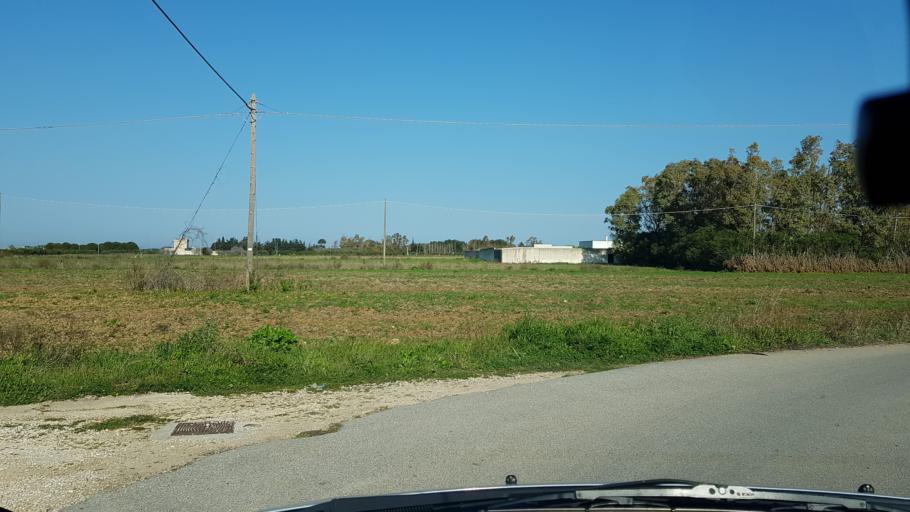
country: IT
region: Apulia
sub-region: Provincia di Brindisi
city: Brindisi
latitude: 40.6586
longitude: 17.9201
